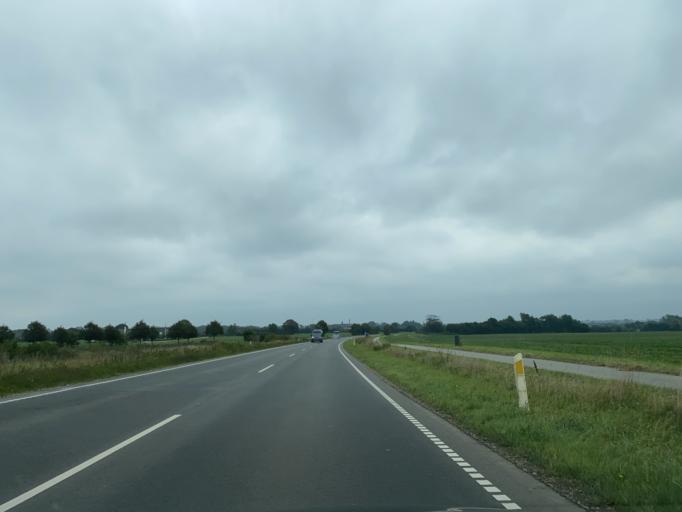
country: DK
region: South Denmark
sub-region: Kolding Kommune
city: Christiansfeld
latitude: 55.3599
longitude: 9.4611
